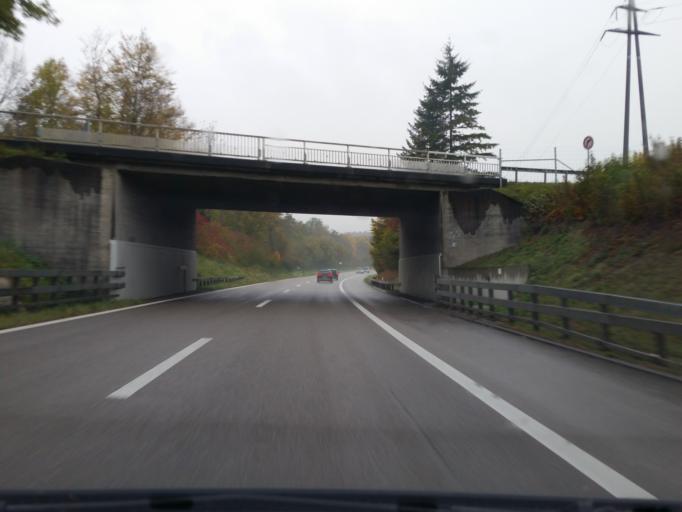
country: CH
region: Zurich
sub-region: Bezirk Winterthur
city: Sulz
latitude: 47.5343
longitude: 8.8014
